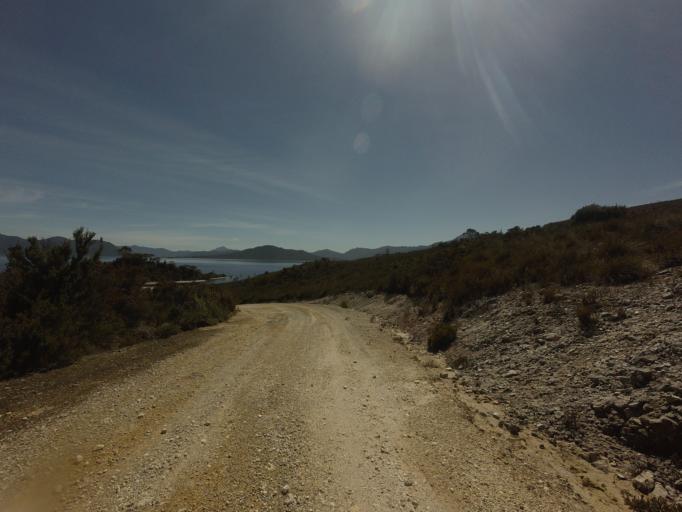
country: AU
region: Tasmania
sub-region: Huon Valley
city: Geeveston
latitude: -43.0333
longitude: 146.3336
